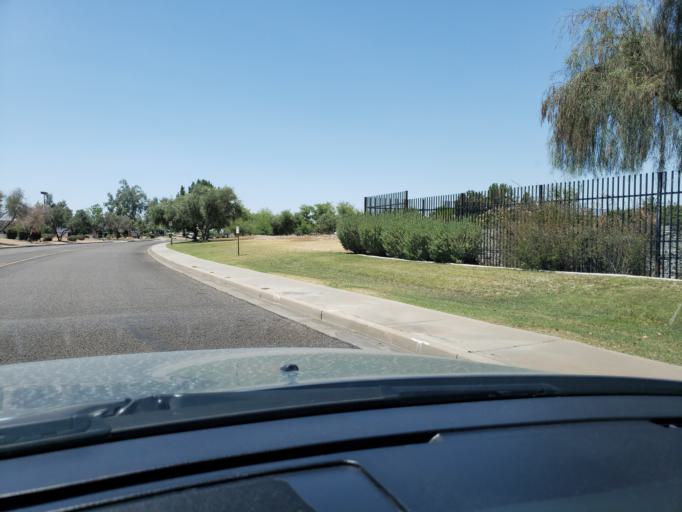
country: US
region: Arizona
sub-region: Maricopa County
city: Glendale
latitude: 33.6288
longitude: -112.1180
